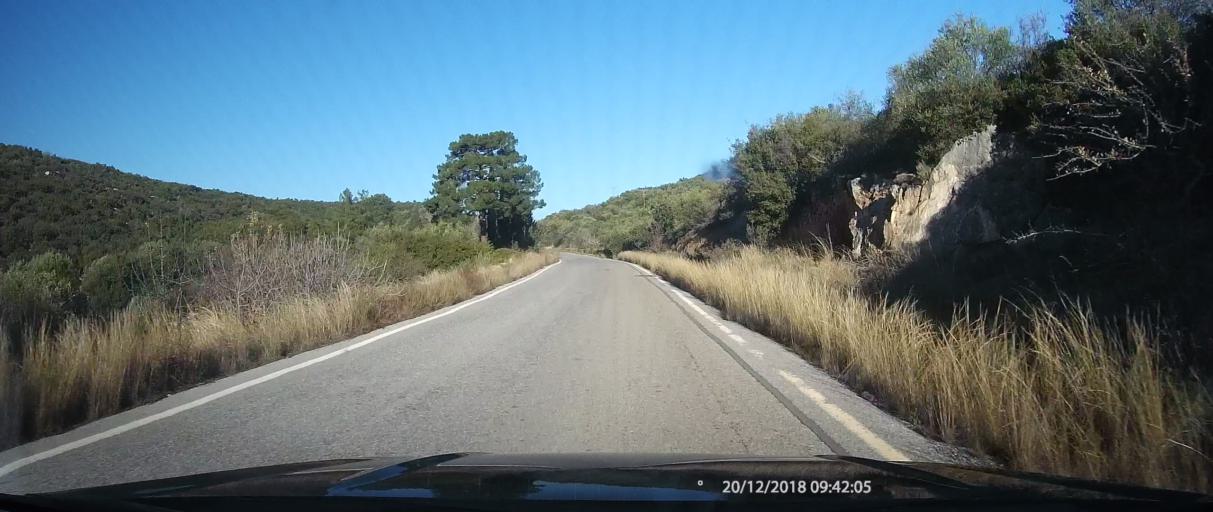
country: GR
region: Peloponnese
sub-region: Nomos Lakonias
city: Yerakion
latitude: 36.9558
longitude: 22.7588
